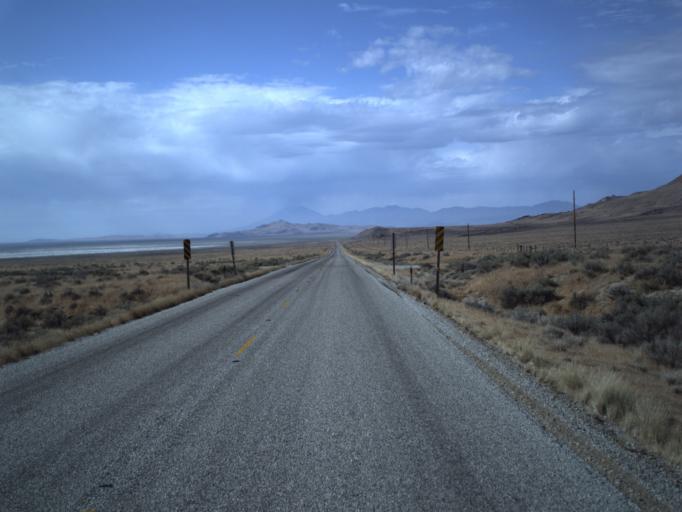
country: US
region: Utah
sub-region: Tooele County
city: Wendover
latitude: 41.4877
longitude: -113.6220
